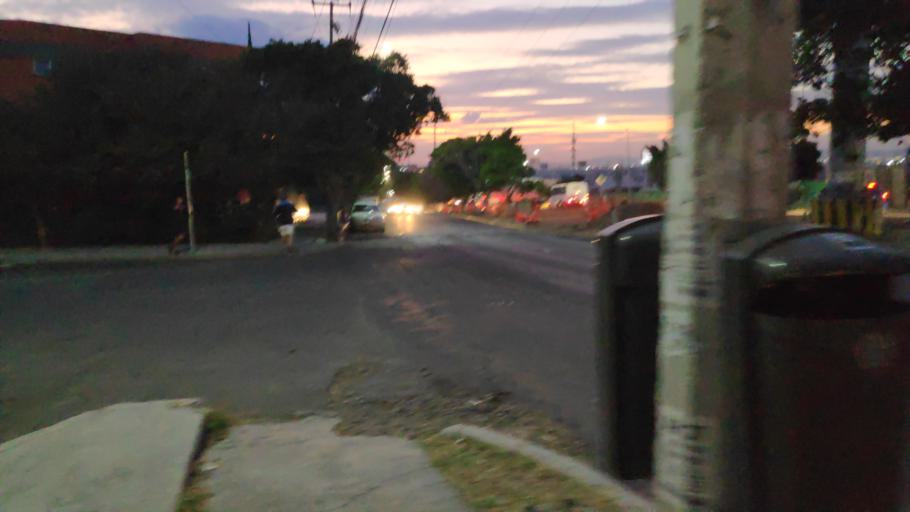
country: MX
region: Queretaro
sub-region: Queretaro
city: Santiago de Queretaro
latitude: 20.5781
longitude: -100.3709
